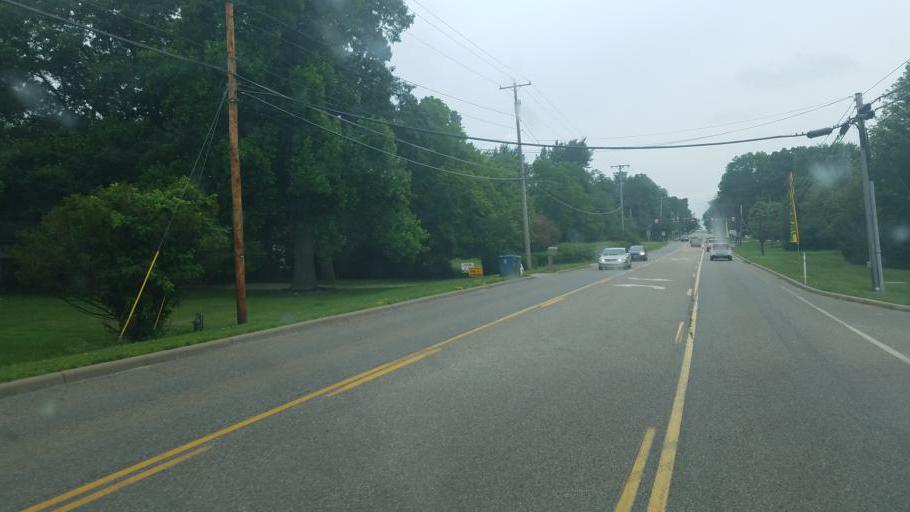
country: US
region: Ohio
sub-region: Summit County
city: Tallmadge
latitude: 41.1009
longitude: -81.4133
